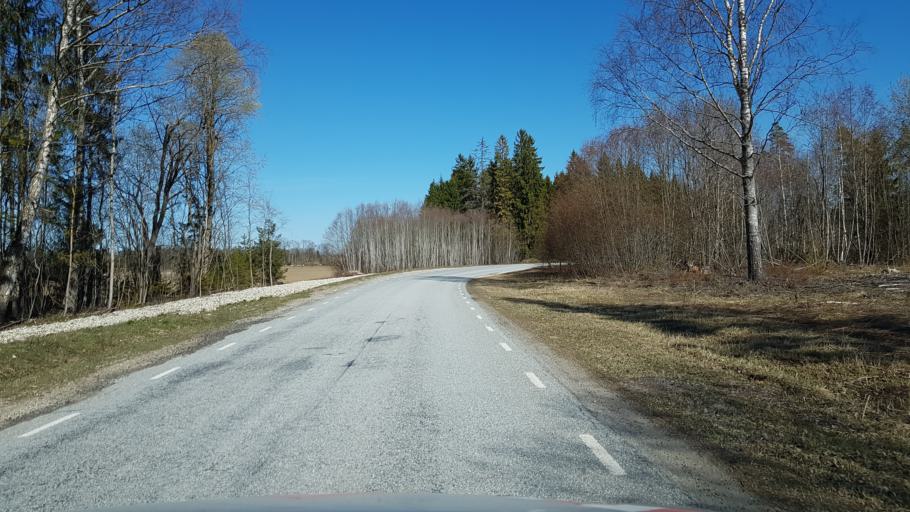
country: EE
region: Laeaene-Virumaa
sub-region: Viru-Nigula vald
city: Kunda
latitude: 59.3376
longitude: 26.6537
